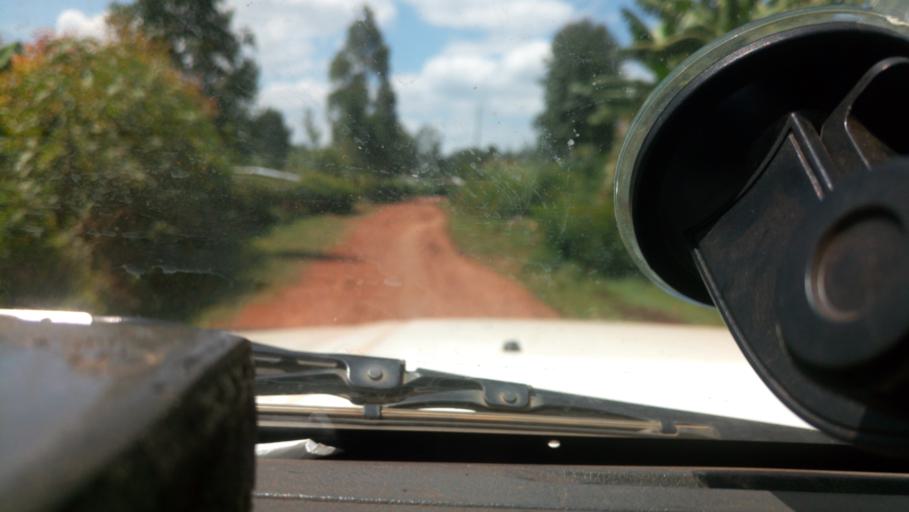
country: KE
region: Kisii
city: Ogembo
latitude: -0.8624
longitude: 34.7382
